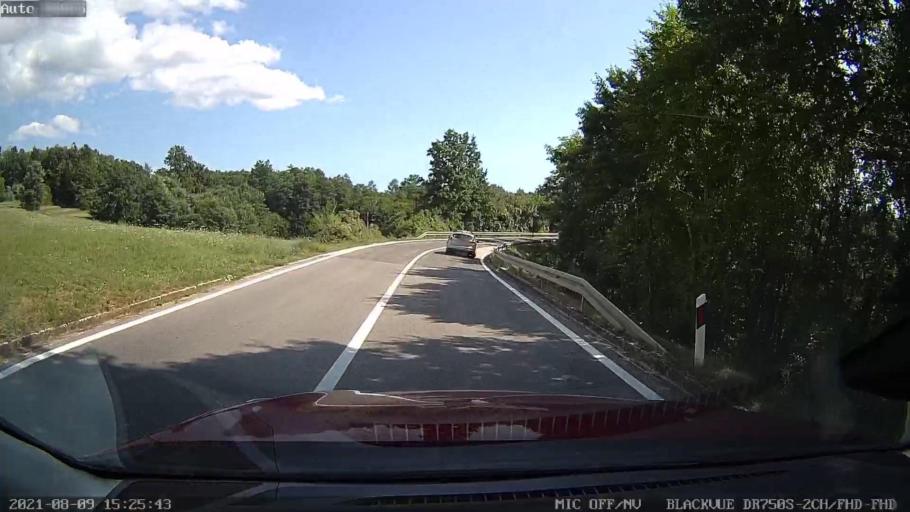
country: HR
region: Istarska
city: Pazin
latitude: 45.1672
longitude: 13.9089
